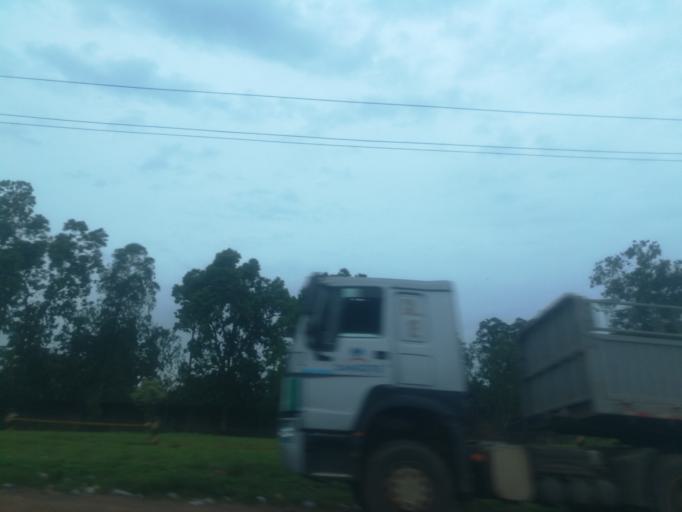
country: NG
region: Oyo
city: Ibadan
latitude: 7.3937
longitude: 3.9689
